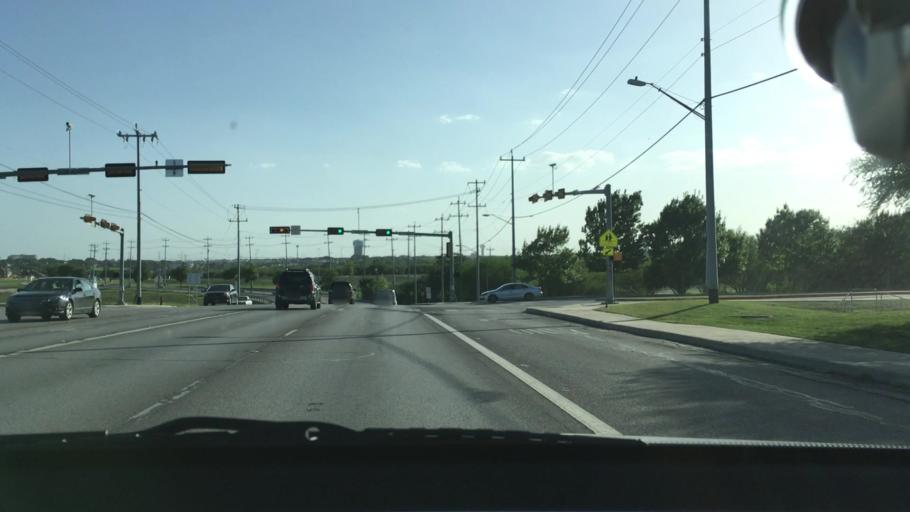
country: US
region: Texas
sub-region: Bexar County
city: Live Oak
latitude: 29.5443
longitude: -98.3201
